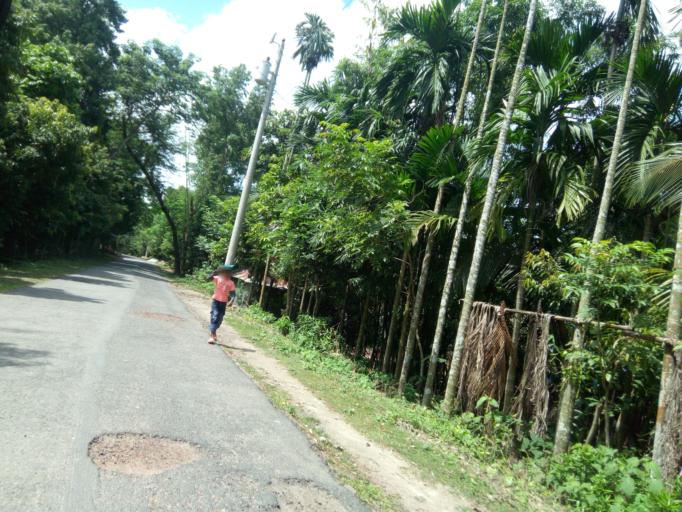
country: BD
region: Khulna
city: Kalia
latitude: 23.0158
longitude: 89.7185
